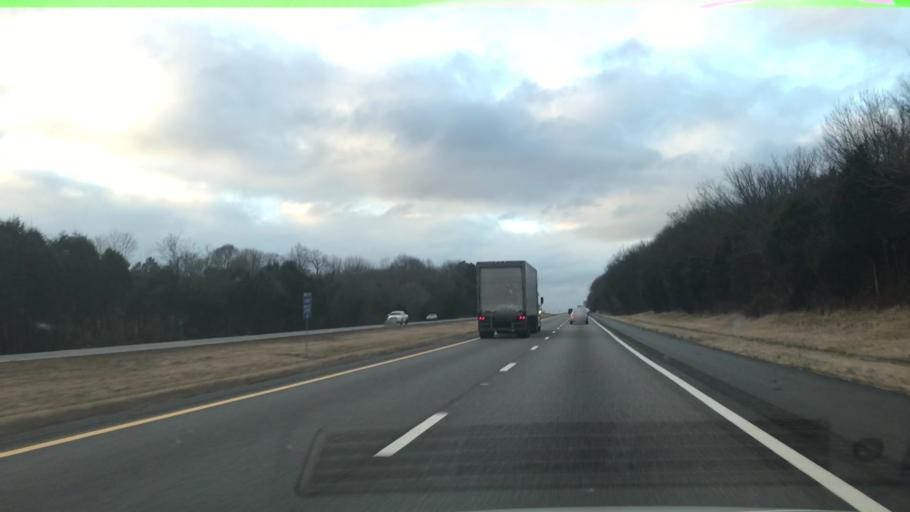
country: US
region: Tennessee
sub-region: Wilson County
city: Watertown
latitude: 36.1792
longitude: -86.1459
